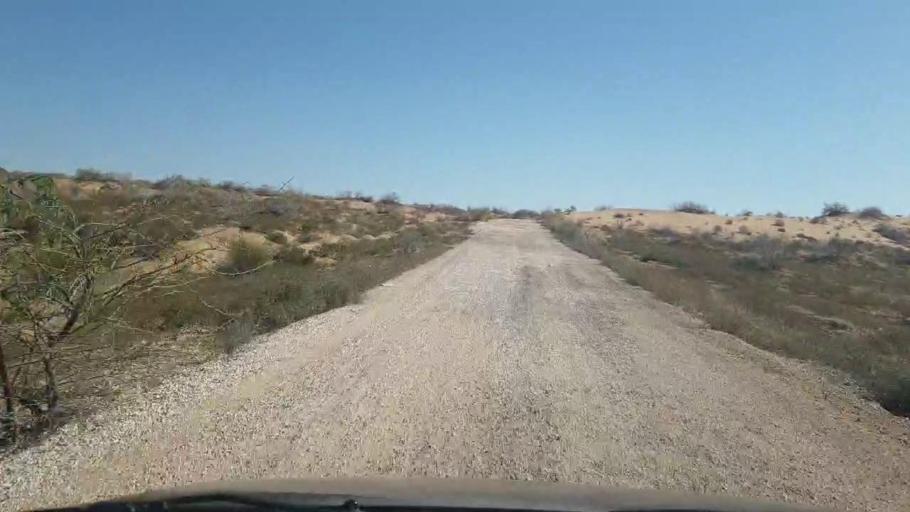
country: PK
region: Sindh
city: Bozdar
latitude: 27.0185
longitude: 68.7322
